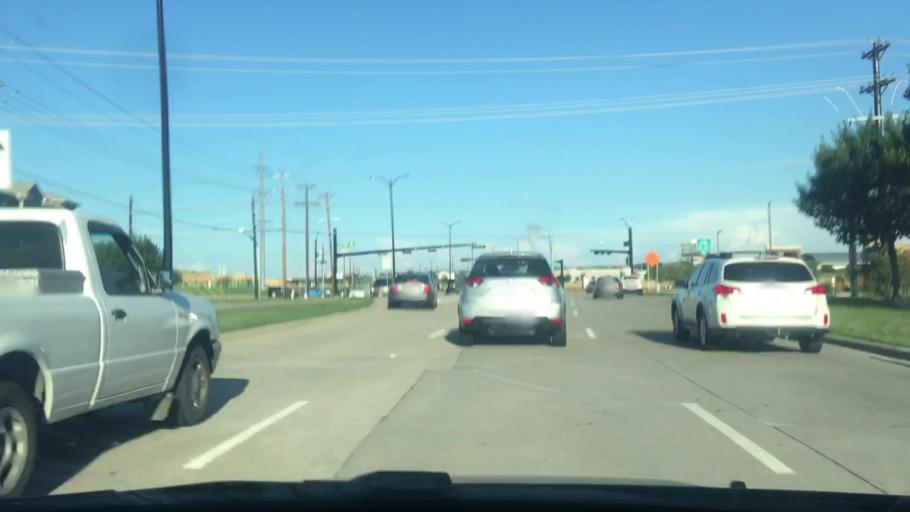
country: US
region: Texas
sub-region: Collin County
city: Frisco
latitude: 33.1750
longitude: -96.8338
